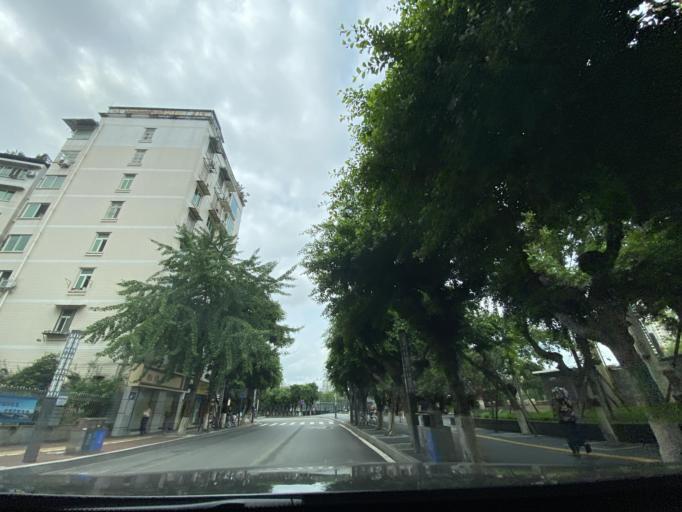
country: CN
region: Sichuan
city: Jiancheng
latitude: 30.3925
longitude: 104.5550
